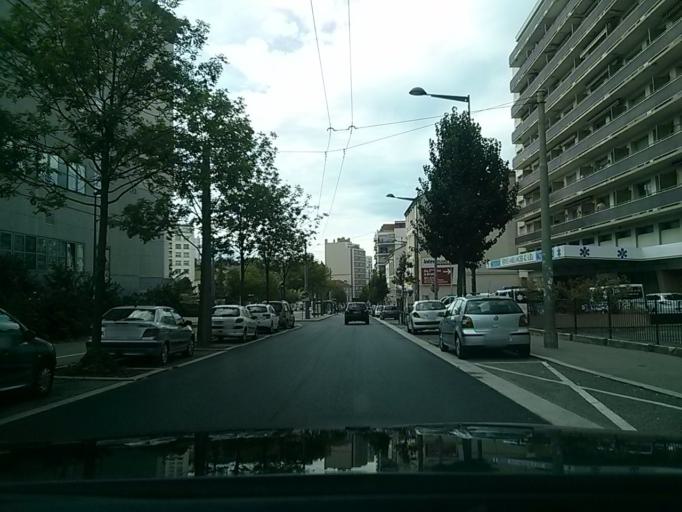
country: FR
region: Rhone-Alpes
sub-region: Departement de la Loire
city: Saint-Etienne
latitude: 45.4144
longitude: 4.3954
